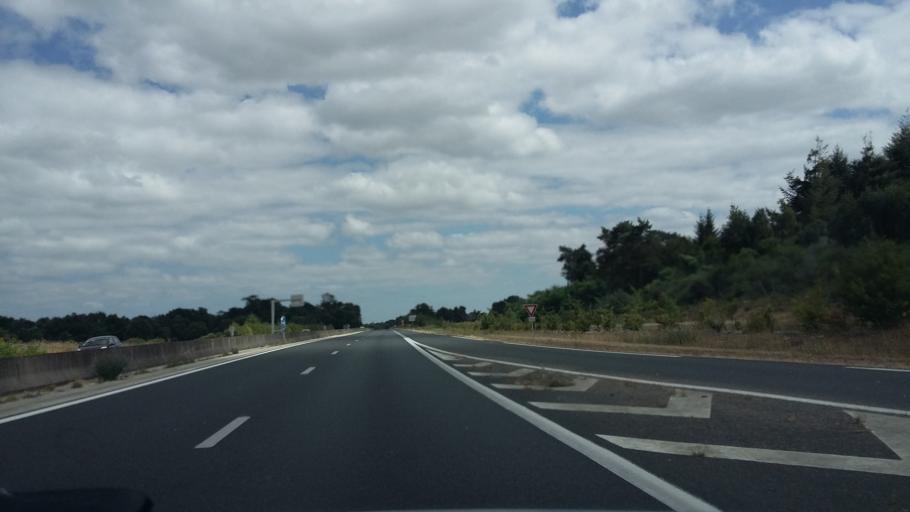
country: FR
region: Pays de la Loire
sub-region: Departement de la Vendee
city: Bournezeau
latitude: 46.6437
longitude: -1.1995
